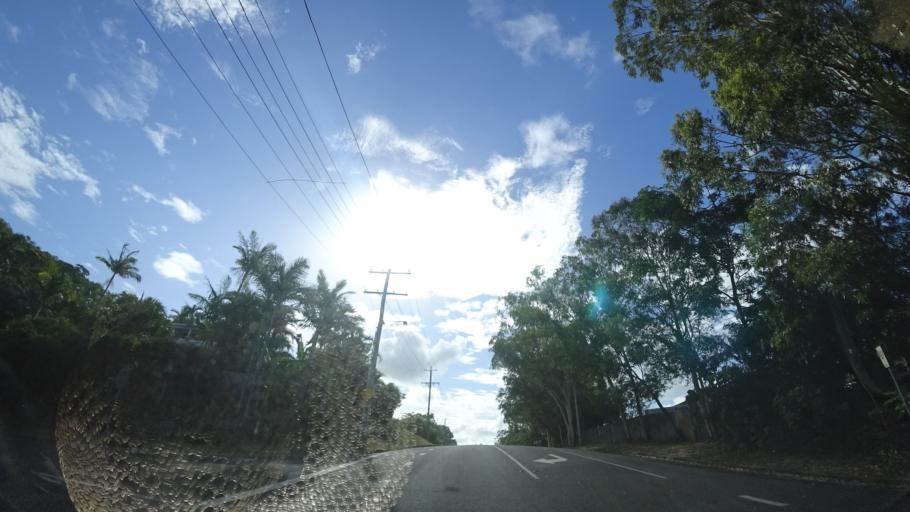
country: AU
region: Queensland
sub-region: Sunshine Coast
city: Coolum Beach
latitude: -26.5566
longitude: 153.0850
